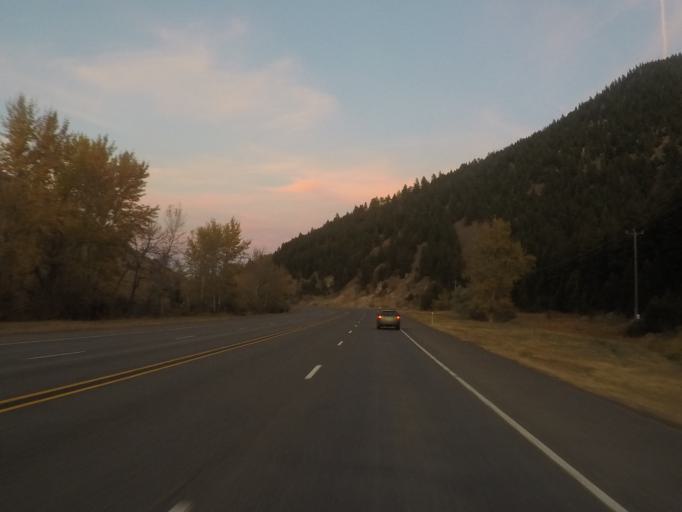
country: US
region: Montana
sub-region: Lewis and Clark County
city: Helena West Side
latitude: 46.5894
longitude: -112.1209
